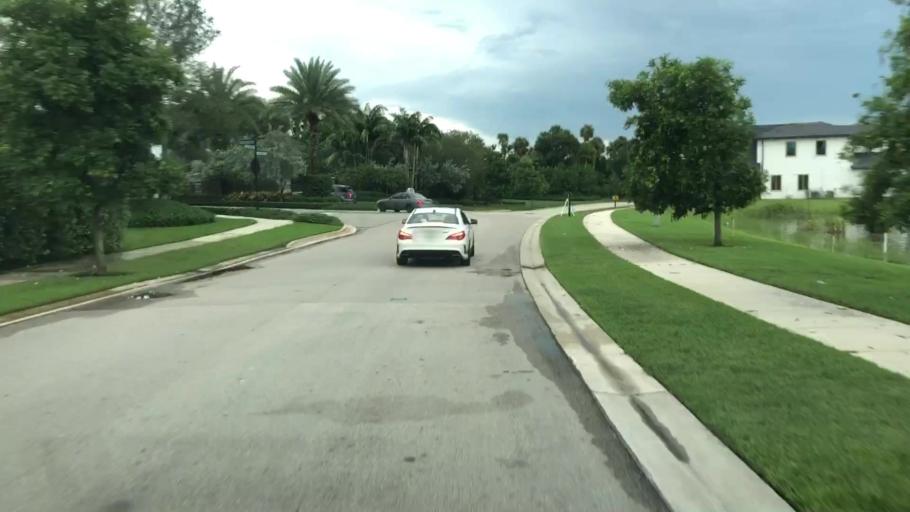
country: US
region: Florida
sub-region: Broward County
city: Parkland
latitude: 26.3359
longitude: -80.2757
